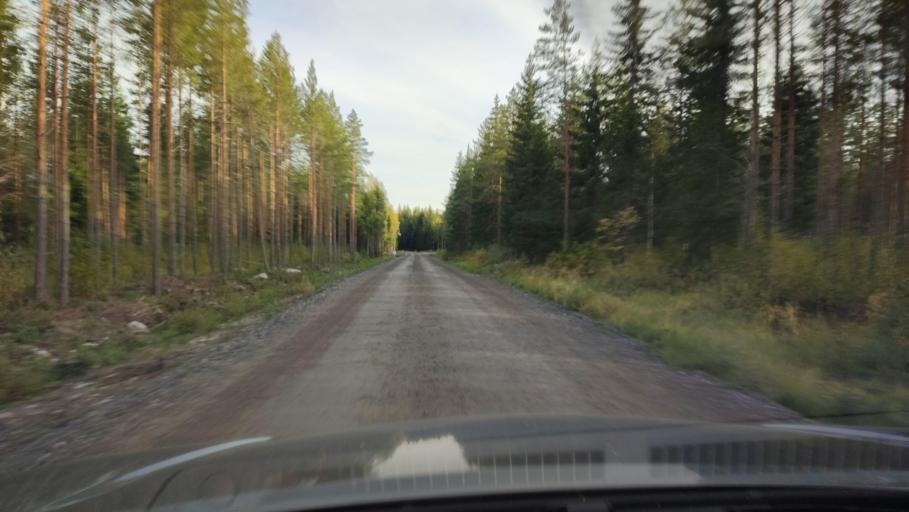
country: FI
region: Southern Ostrobothnia
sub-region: Suupohja
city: Karijoki
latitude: 62.1699
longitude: 21.5943
